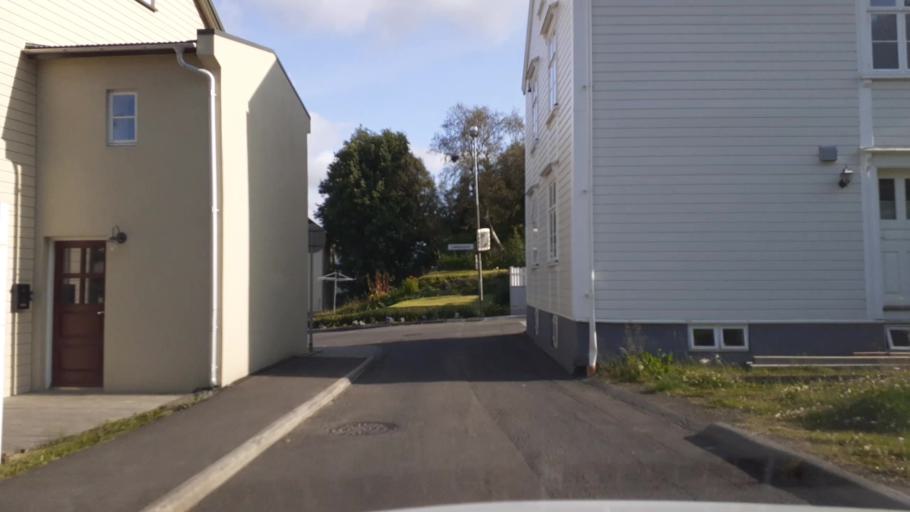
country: IS
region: Northeast
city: Akureyri
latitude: 65.6720
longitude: -18.0880
